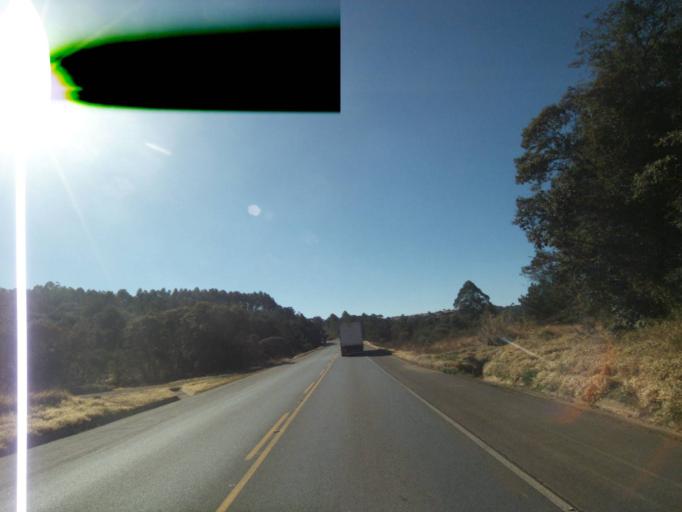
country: BR
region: Parana
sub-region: Tibagi
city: Tibagi
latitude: -24.5891
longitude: -50.4369
